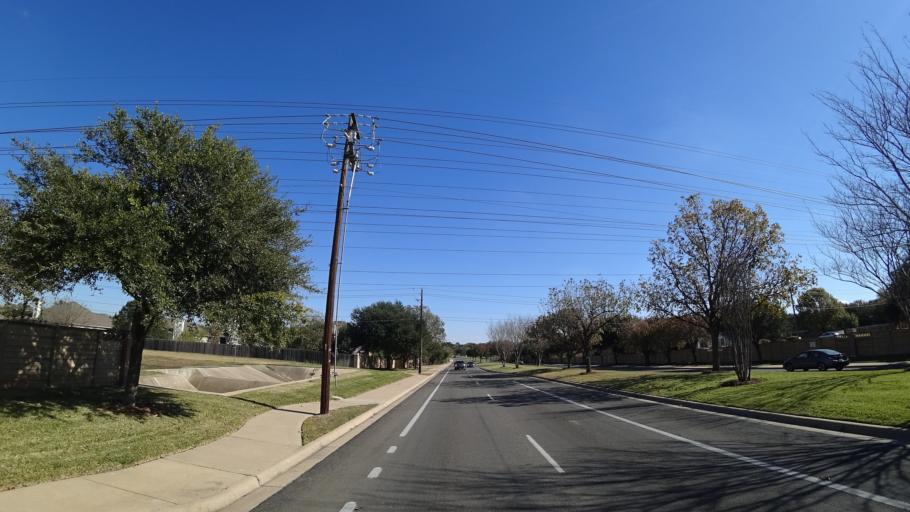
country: US
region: Texas
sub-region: Travis County
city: Wells Branch
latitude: 30.4282
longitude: -97.6887
